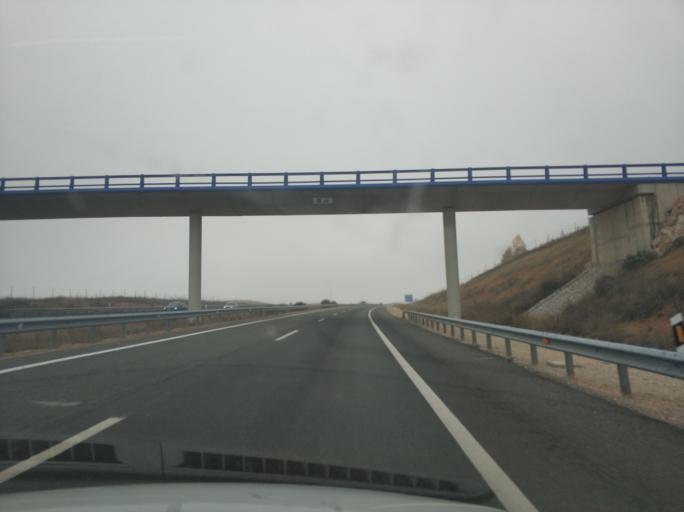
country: ES
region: Castille and Leon
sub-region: Provincia de Soria
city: Adradas
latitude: 41.3641
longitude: -2.4699
